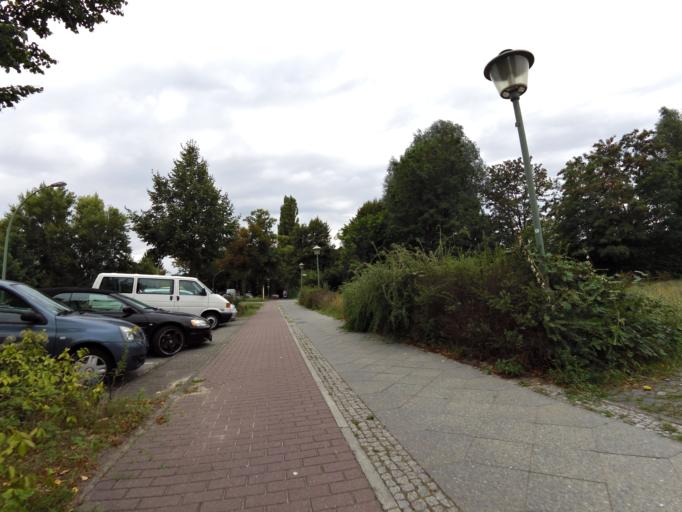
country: DE
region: Berlin
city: Plaenterwald
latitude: 52.4735
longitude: 13.4707
